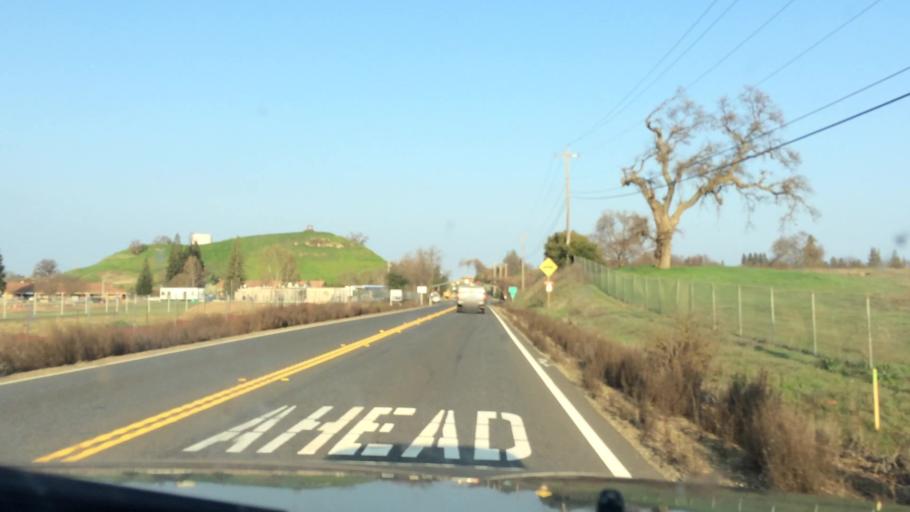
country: US
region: California
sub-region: Sacramento County
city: Rancho Murieta
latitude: 38.4948
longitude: -121.0956
